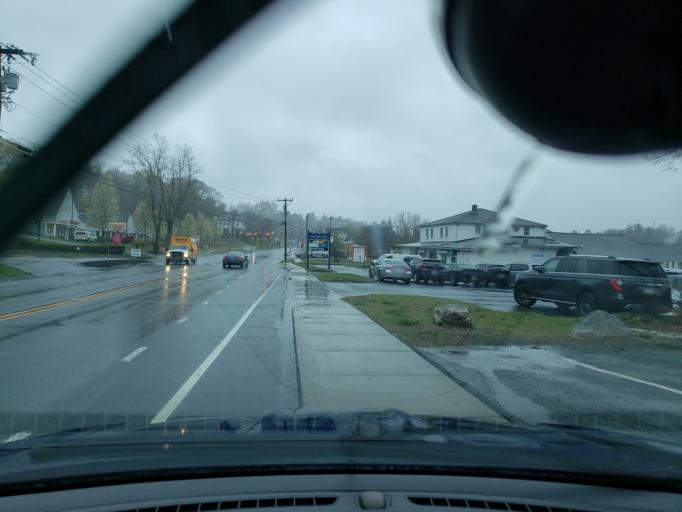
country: US
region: Connecticut
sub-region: Litchfield County
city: Watertown
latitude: 41.5926
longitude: -73.1084
